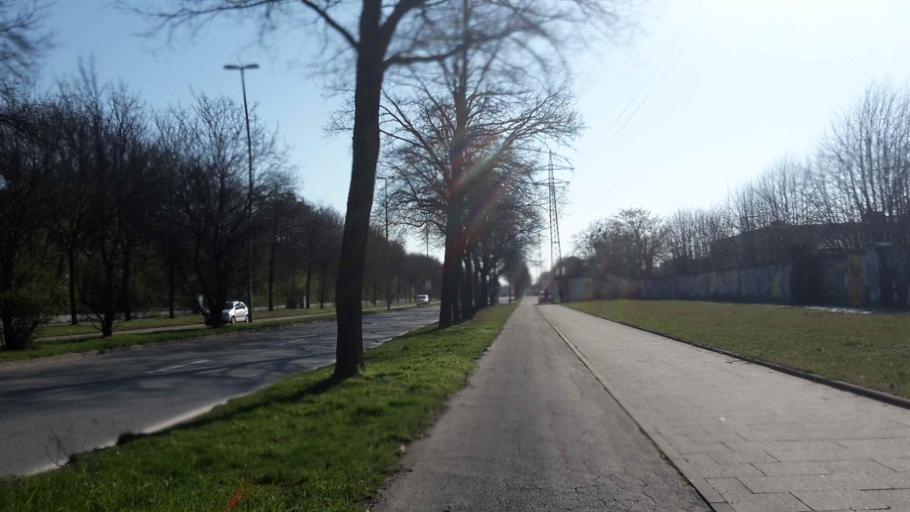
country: DE
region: Bavaria
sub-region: Upper Bavaria
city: Unterfoehring
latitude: 48.2013
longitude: 11.5986
